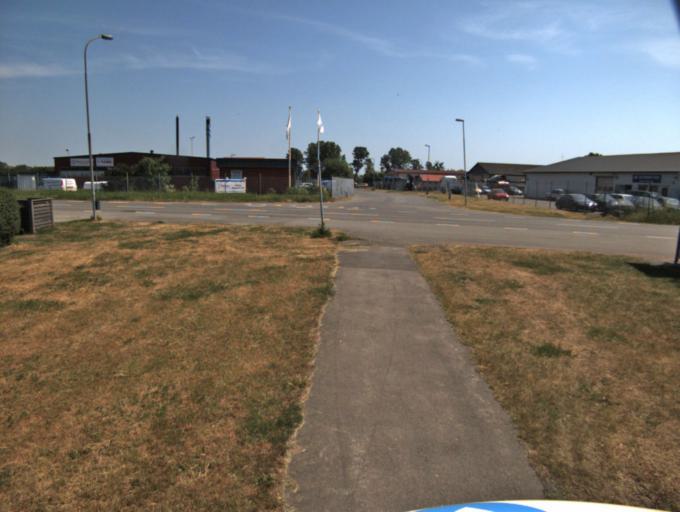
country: SE
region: Skane
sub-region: Kristianstads Kommun
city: Fjalkinge
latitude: 56.0458
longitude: 14.2785
